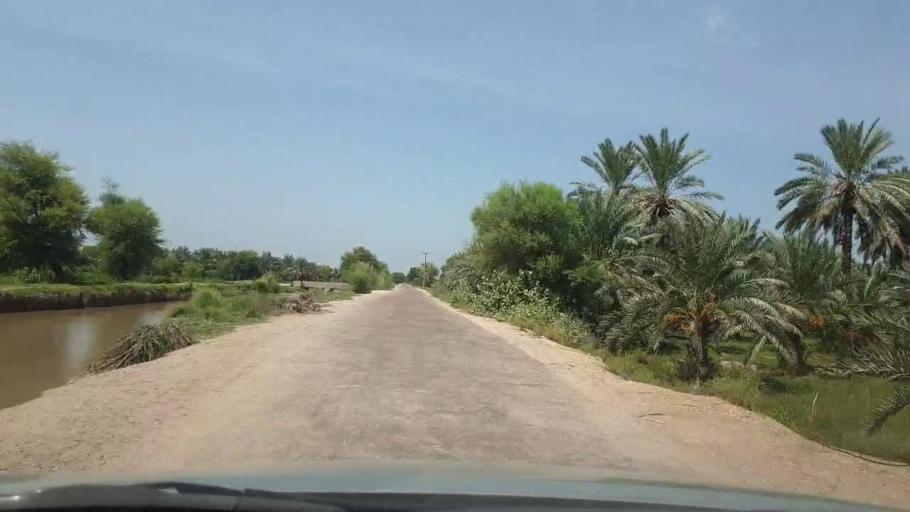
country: PK
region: Sindh
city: Pano Aqil
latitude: 27.6810
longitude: 69.1098
